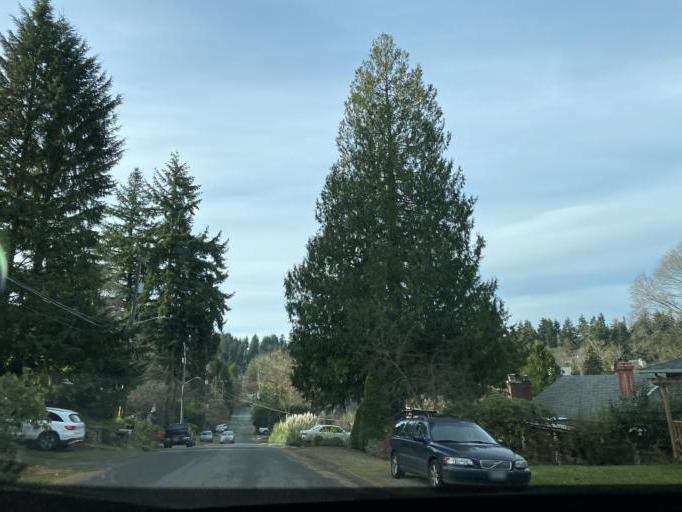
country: US
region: Washington
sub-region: King County
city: Lake Forest Park
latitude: 47.7003
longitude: -122.2988
